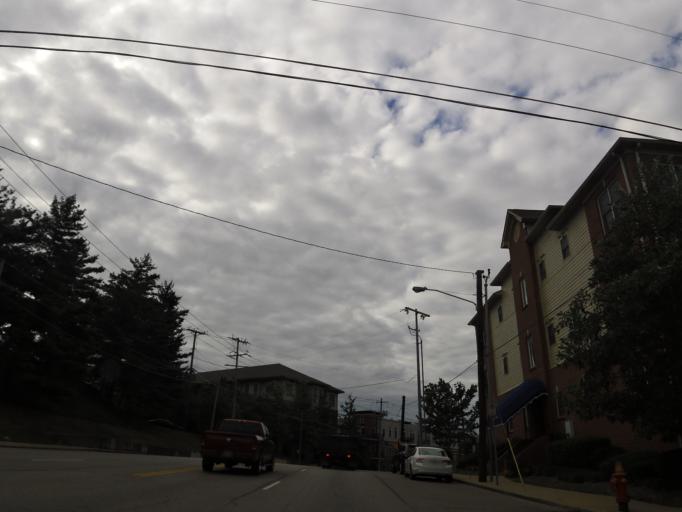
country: US
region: Tennessee
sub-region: Davidson County
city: Nashville
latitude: 36.1436
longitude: -86.8161
